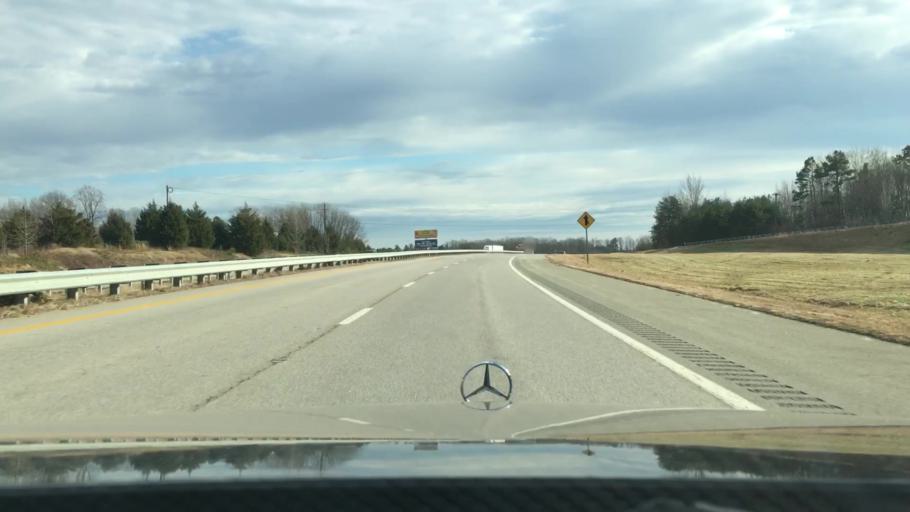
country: US
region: Virginia
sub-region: Pittsylvania County
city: Mount Hermon
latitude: 36.6981
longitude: -79.3636
